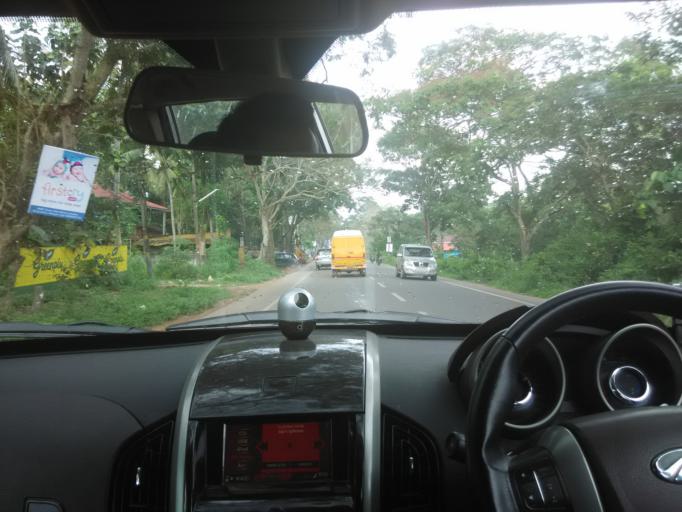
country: IN
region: Kerala
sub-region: Thiruvananthapuram
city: Attingal
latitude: 8.6446
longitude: 76.8430
